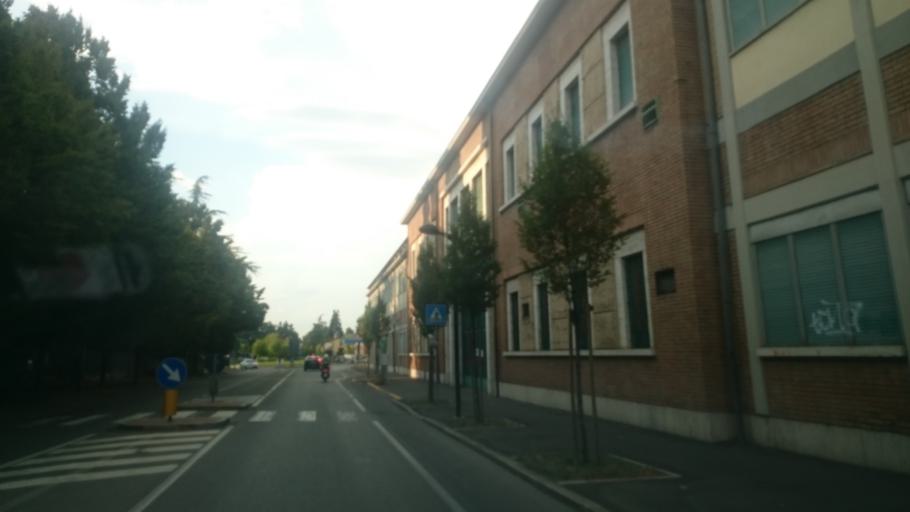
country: IT
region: Emilia-Romagna
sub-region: Provincia di Reggio Emilia
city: Reggio nell'Emilia
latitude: 44.7072
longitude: 10.6255
